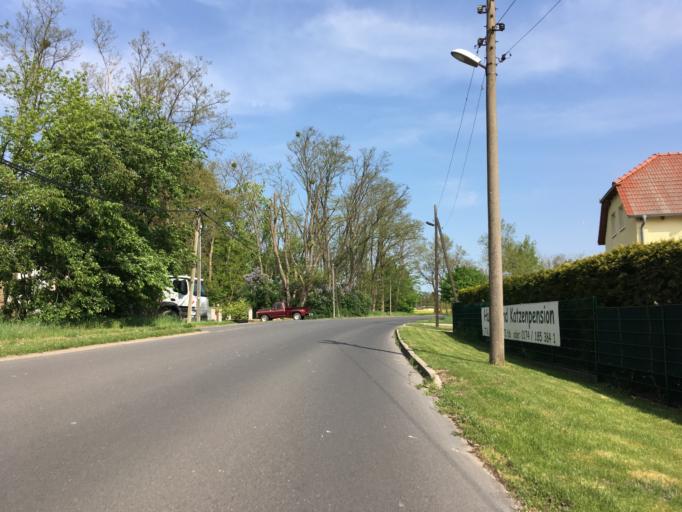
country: DE
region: Brandenburg
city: Altlandsberg
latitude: 52.5772
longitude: 13.7253
